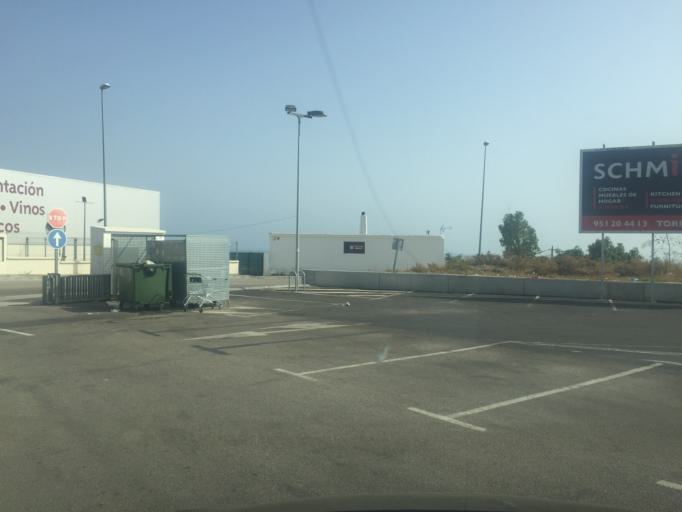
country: ES
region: Andalusia
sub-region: Provincia de Malaga
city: Nerja
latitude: 36.7543
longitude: -3.8841
